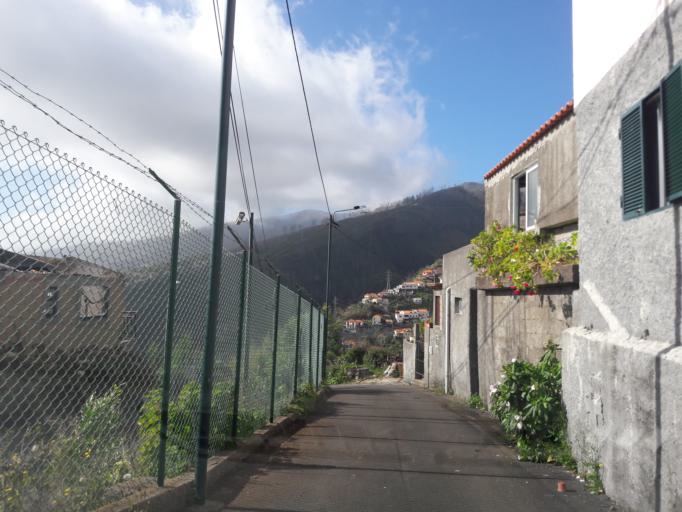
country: PT
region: Madeira
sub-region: Funchal
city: Nossa Senhora do Monte
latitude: 32.6720
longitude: -16.8892
